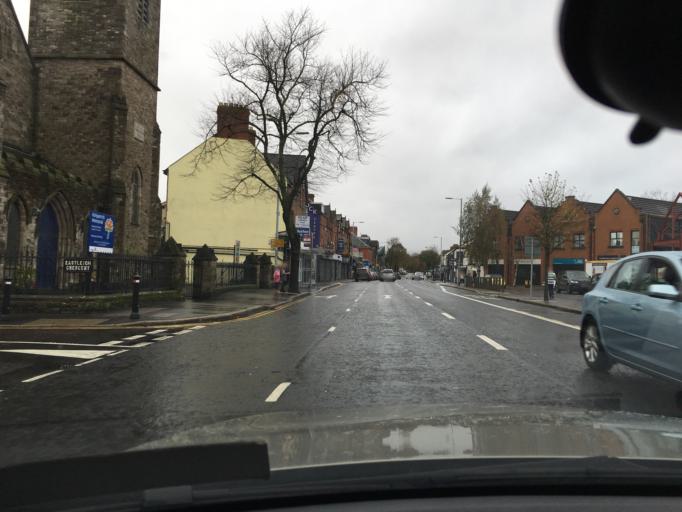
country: GB
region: Northern Ireland
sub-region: Castlereagh District
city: Castlereagh
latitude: 54.5951
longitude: -5.8667
